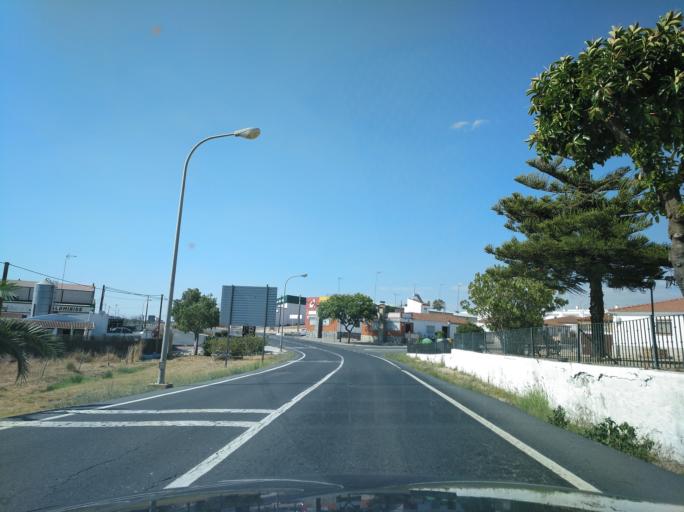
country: ES
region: Andalusia
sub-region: Provincia de Huelva
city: Alosno
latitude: 37.5501
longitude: -7.1200
